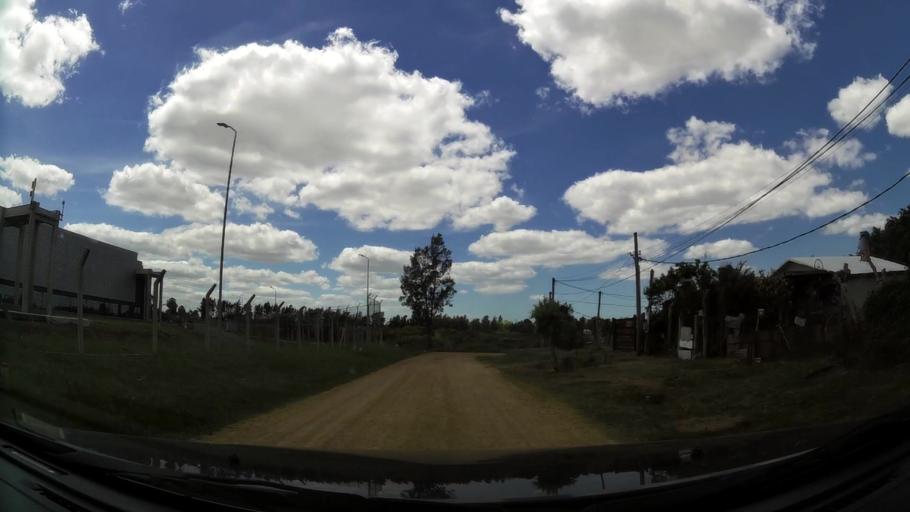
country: UY
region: Canelones
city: Colonia Nicolich
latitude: -34.8175
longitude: -56.0051
